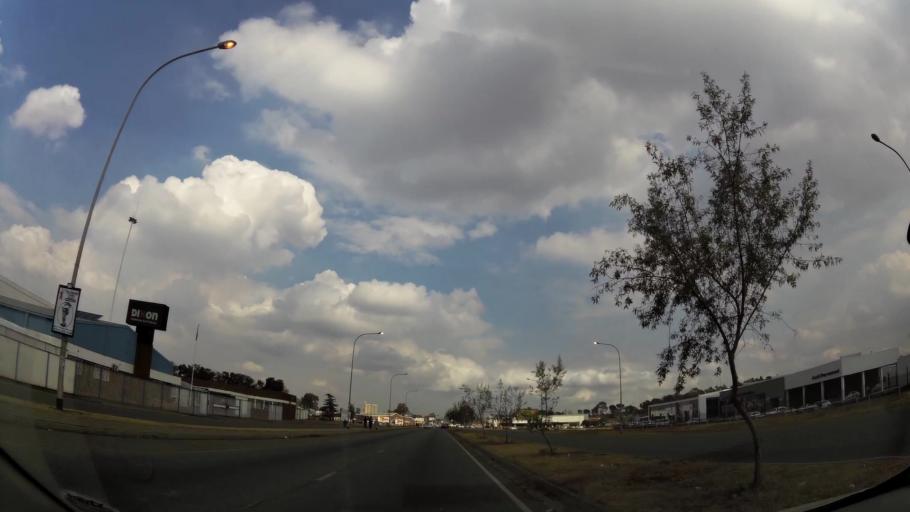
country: ZA
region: Gauteng
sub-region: Sedibeng District Municipality
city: Vereeniging
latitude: -26.6599
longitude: 27.9350
